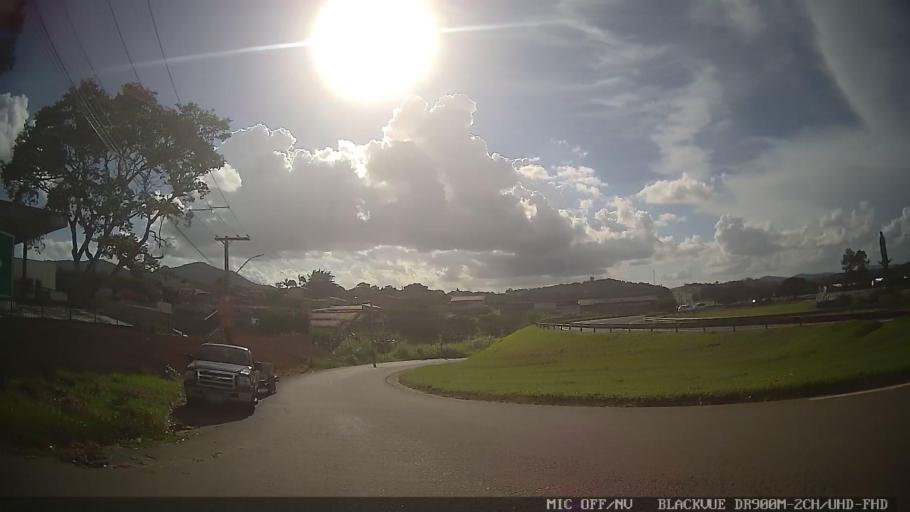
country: BR
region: Sao Paulo
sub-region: Bom Jesus Dos Perdoes
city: Bom Jesus dos Perdoes
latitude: -23.1175
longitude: -46.4833
